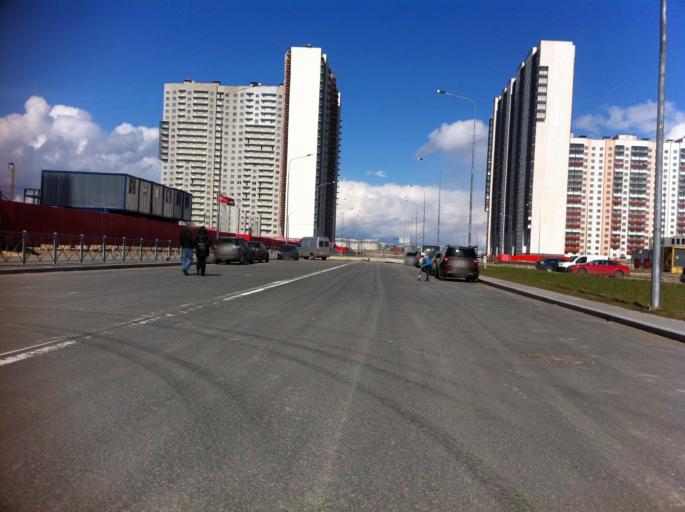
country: RU
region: St.-Petersburg
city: Uritsk
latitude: 59.8676
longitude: 30.1578
